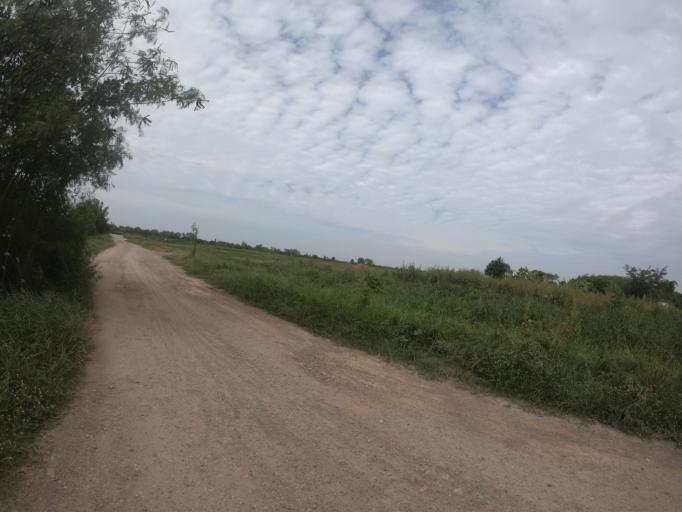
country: TH
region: Pathum Thani
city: Ban Lam Luk Ka
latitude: 14.0381
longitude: 100.8611
